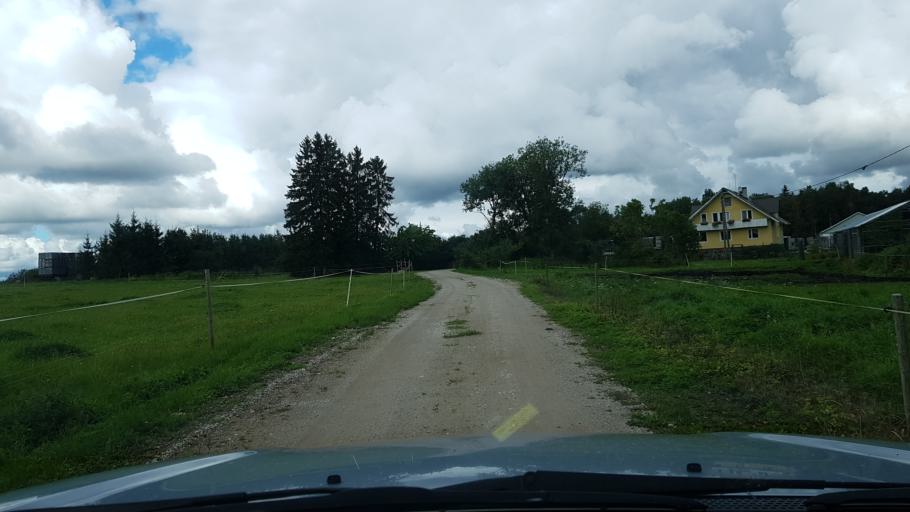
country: EE
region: Harju
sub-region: Raasiku vald
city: Arukula
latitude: 59.2760
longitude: 25.0944
